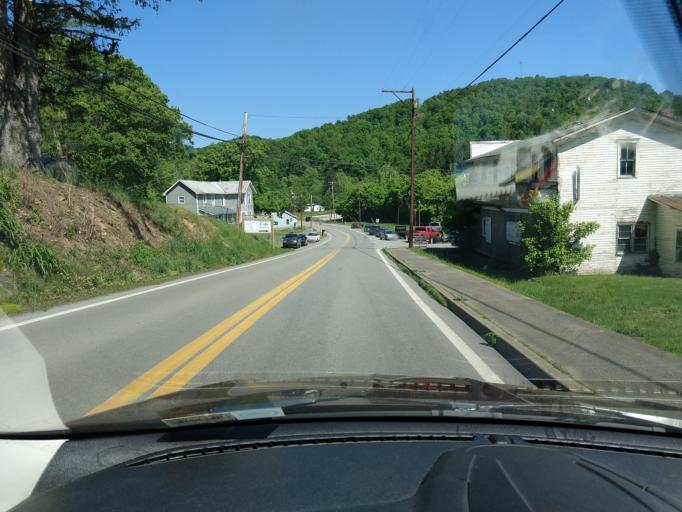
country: US
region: West Virginia
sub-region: Gilmer County
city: Glenville
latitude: 38.9135
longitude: -80.7490
